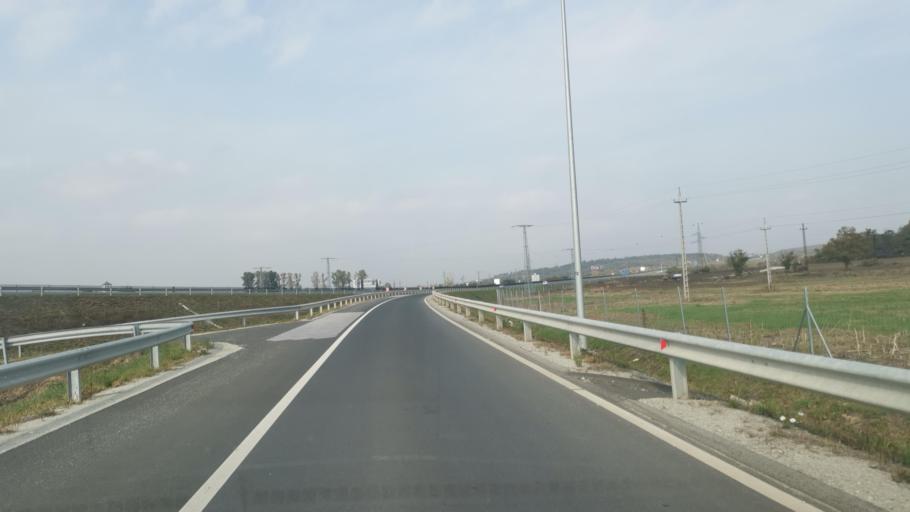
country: HU
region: Gyor-Moson-Sopron
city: Sopron
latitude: 47.6555
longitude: 16.6275
